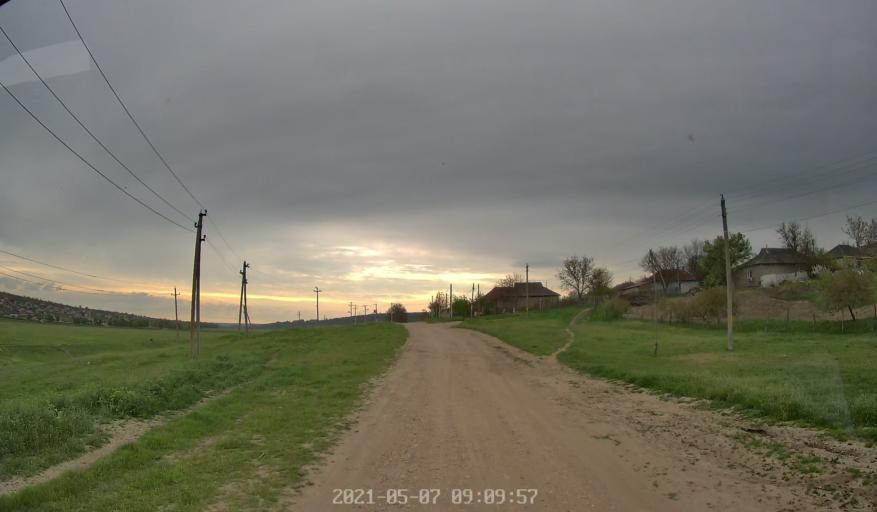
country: MD
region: Chisinau
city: Vadul lui Voda
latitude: 47.1181
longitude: 29.0067
